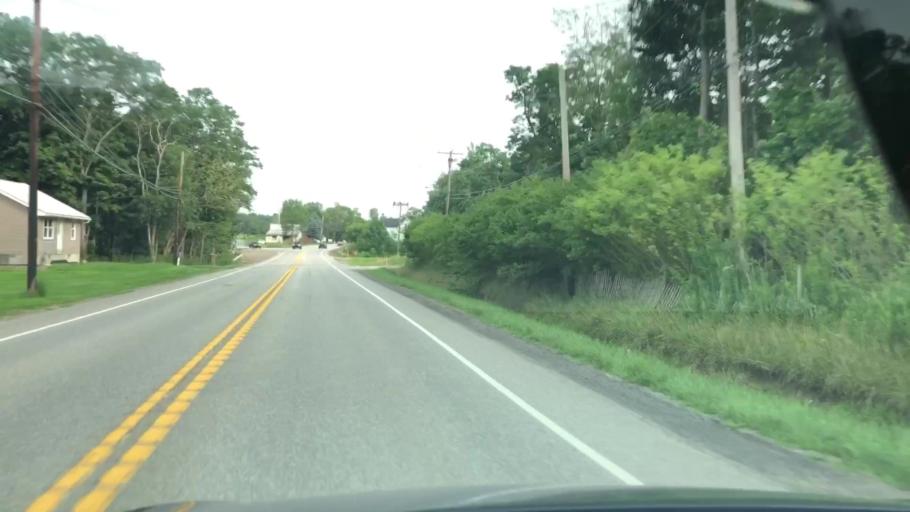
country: US
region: Pennsylvania
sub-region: Erie County
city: Wesleyville
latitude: 42.0794
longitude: -79.9886
